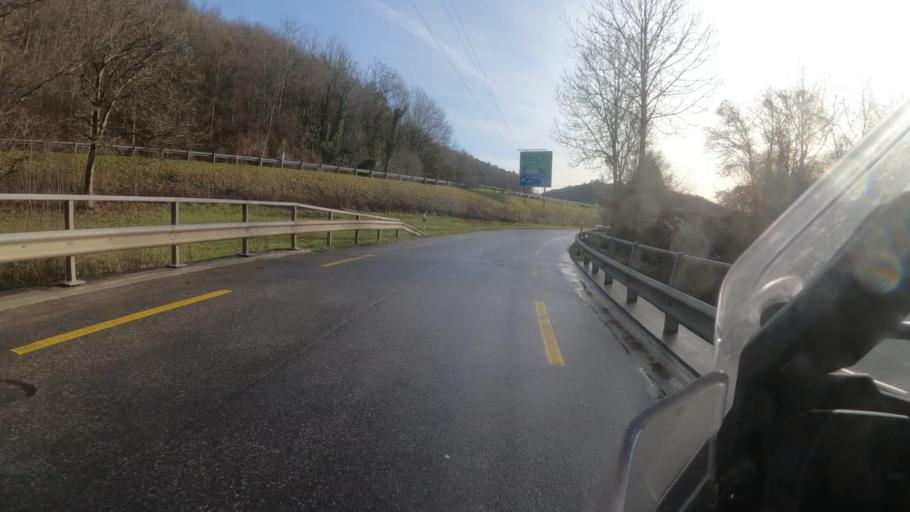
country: CH
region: Schaffhausen
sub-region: Bezirk Schaffhausen
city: Schaffhausen
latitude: 47.7303
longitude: 8.6250
